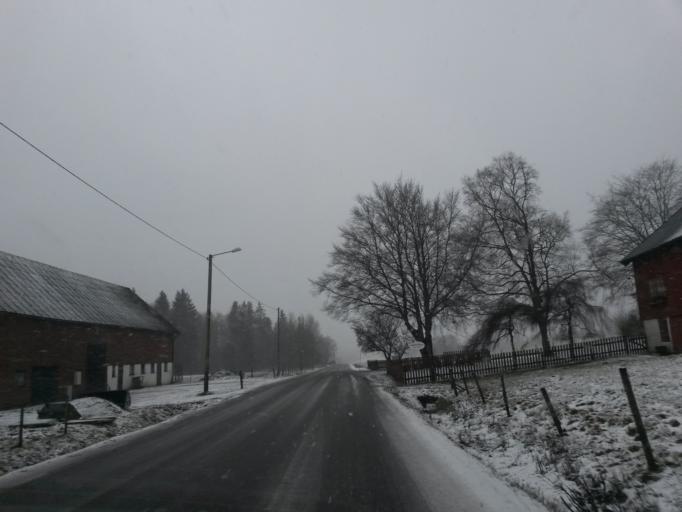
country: SE
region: Vaestra Goetaland
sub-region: Boras Kommun
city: Ganghester
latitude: 57.7544
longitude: 13.0110
